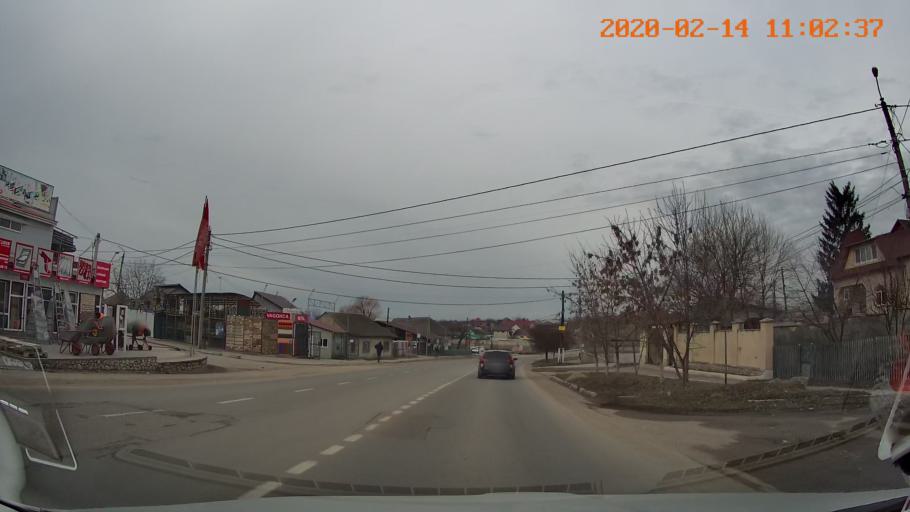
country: MD
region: Raionul Edinet
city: Edinet
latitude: 48.1638
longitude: 27.3170
